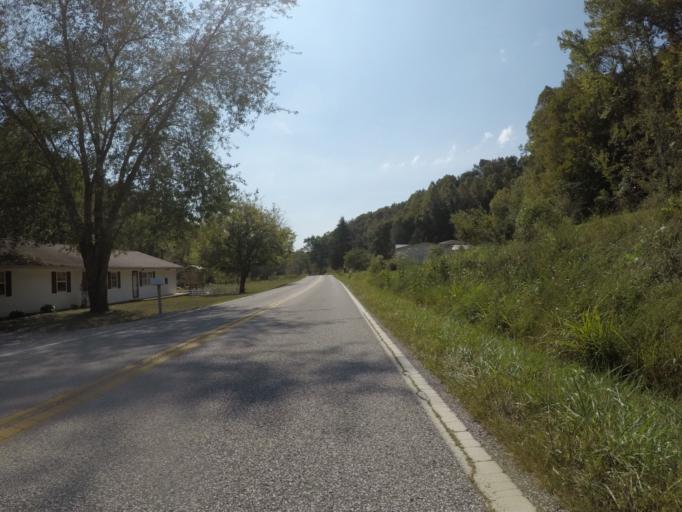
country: US
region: West Virginia
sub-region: Cabell County
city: Lesage
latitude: 38.5637
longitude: -82.3960
